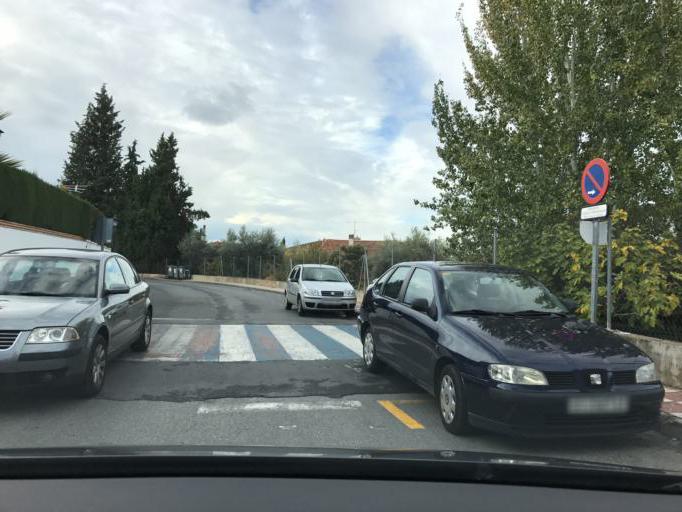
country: ES
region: Andalusia
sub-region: Provincia de Granada
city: Cajar
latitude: 37.1330
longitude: -3.5707
